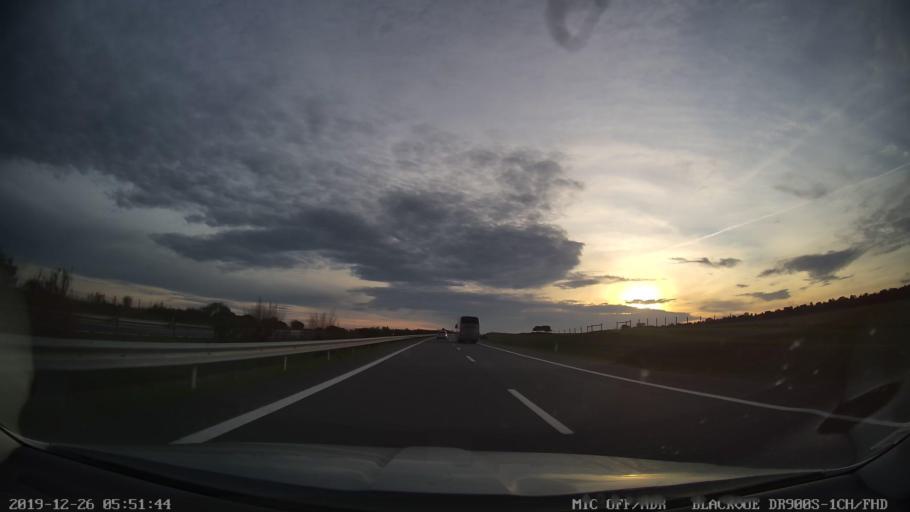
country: PT
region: Evora
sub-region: Evora
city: Evora
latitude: 38.6577
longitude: -7.8446
